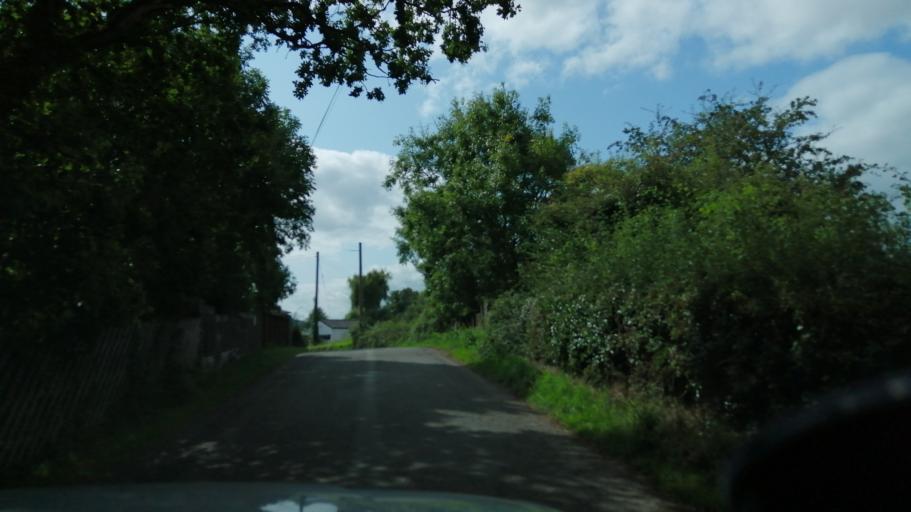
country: GB
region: England
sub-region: Herefordshire
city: Kinnersley
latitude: 52.1339
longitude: -2.9647
